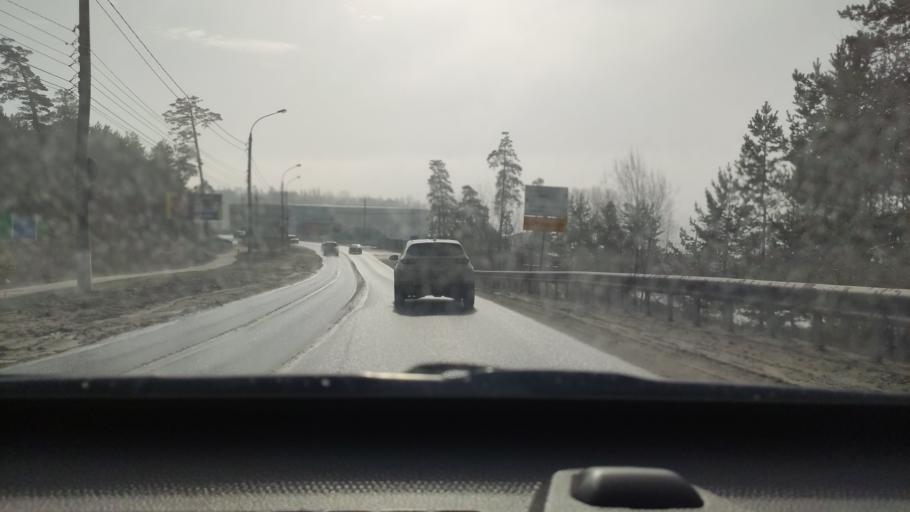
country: RU
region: Samara
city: Tol'yatti
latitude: 53.4735
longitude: 49.3262
